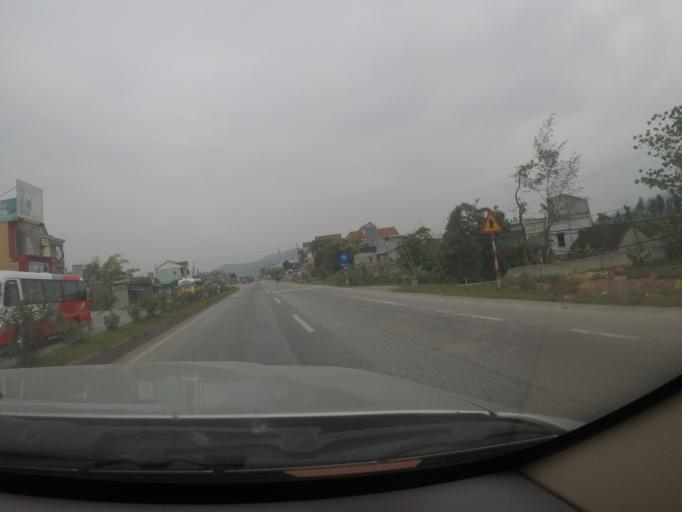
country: VN
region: Nghe An
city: Dien Chau
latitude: 18.9277
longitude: 105.6076
